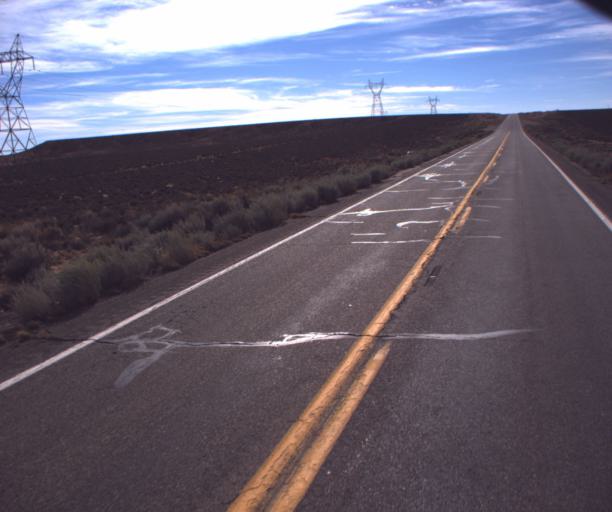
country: US
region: Arizona
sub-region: Coconino County
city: LeChee
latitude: 36.8046
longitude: -111.3054
